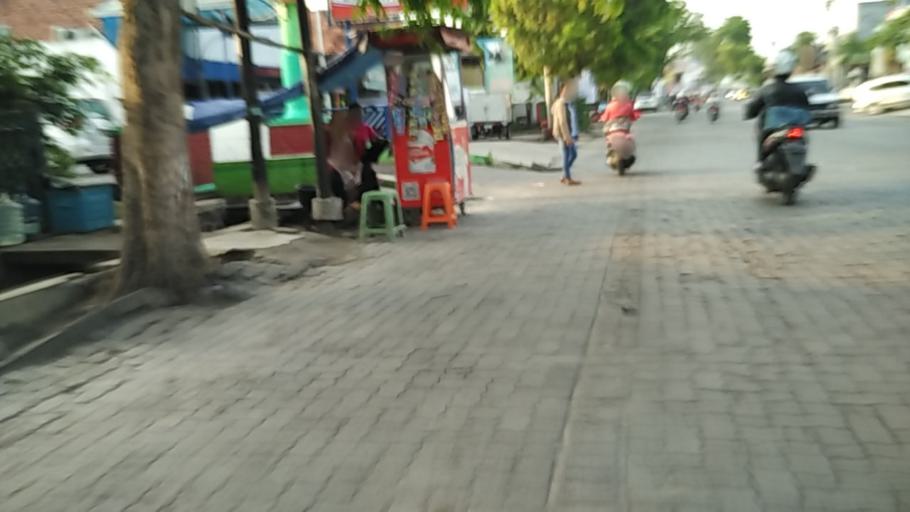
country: ID
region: Central Java
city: Semarang
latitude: -6.9809
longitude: 110.3913
